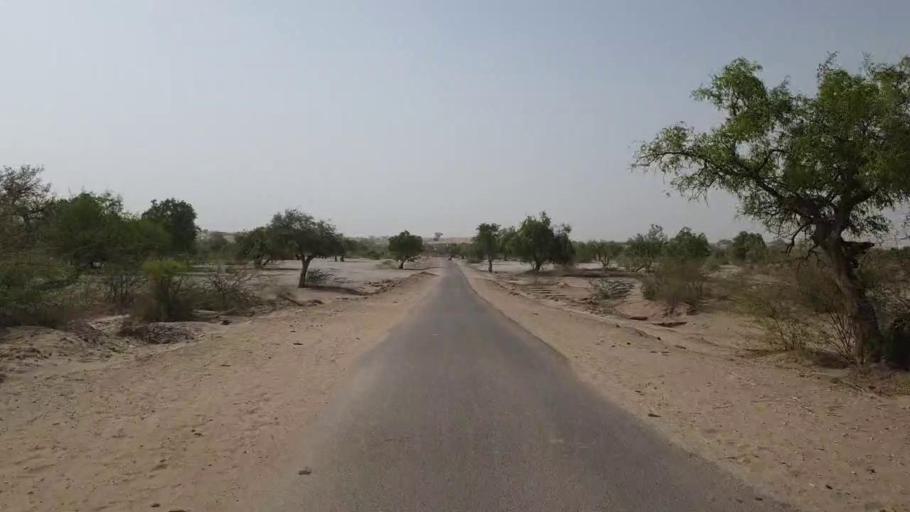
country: PK
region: Sindh
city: Mithi
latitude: 24.6146
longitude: 69.9197
